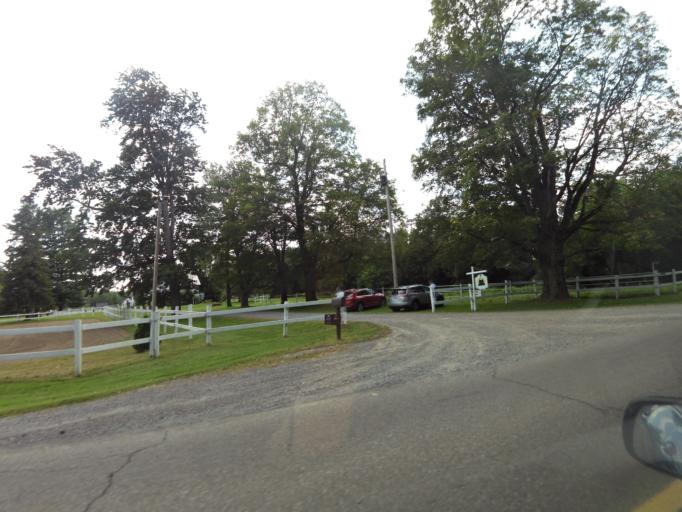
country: CA
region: Ontario
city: Ottawa
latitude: 45.3962
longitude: -75.5762
